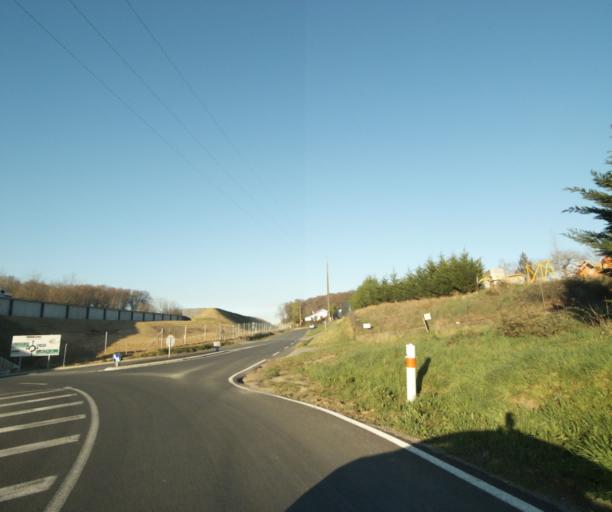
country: FR
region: Aquitaine
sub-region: Departement des Pyrenees-Atlantiques
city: Urrugne
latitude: 43.3622
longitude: -1.6913
